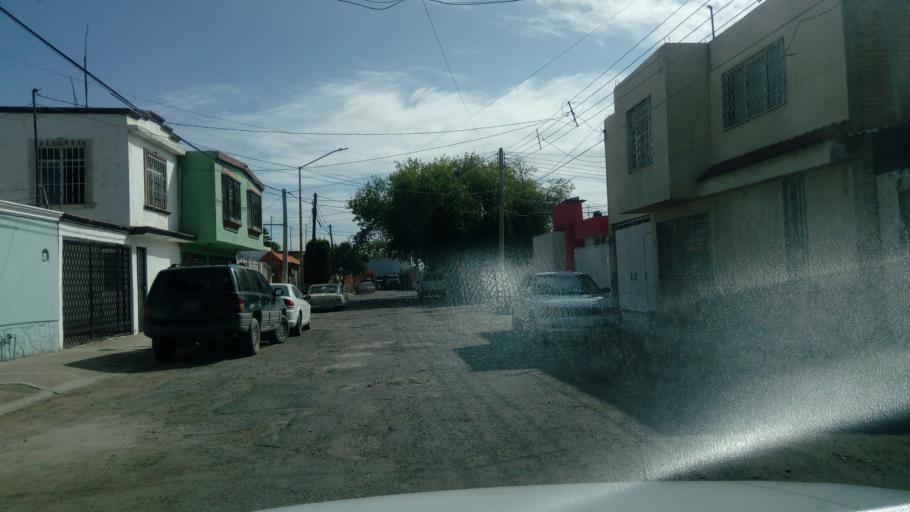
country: MX
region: Durango
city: Victoria de Durango
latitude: 24.0047
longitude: -104.6683
